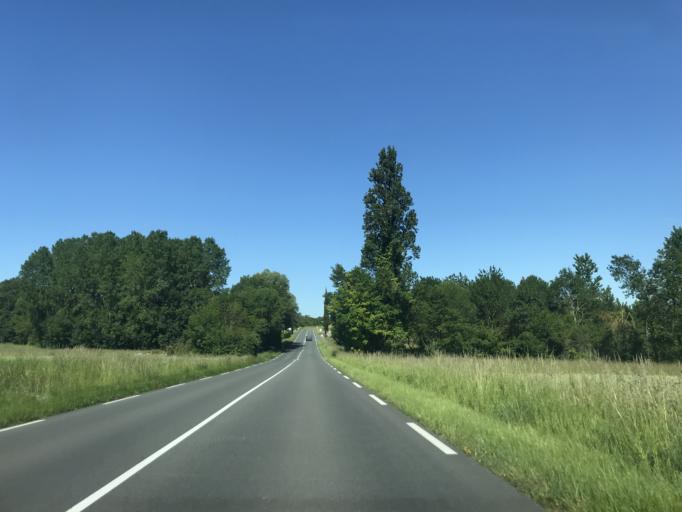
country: FR
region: Poitou-Charentes
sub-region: Departement de la Charente
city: Barbezieux-Saint-Hilaire
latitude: 45.4980
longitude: -0.2437
